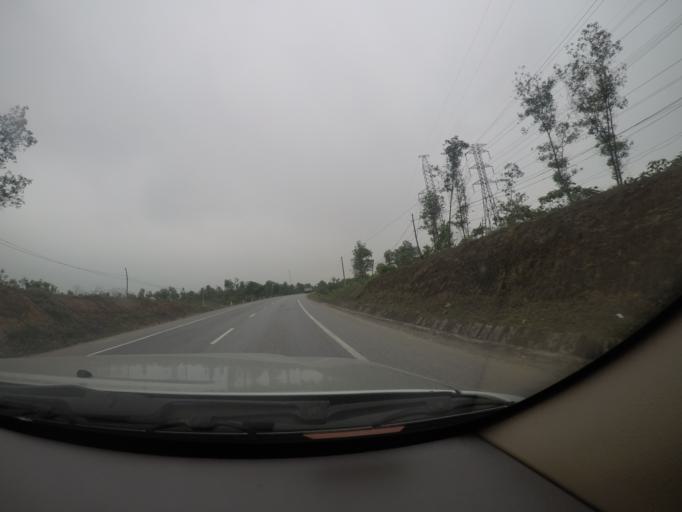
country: VN
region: Ha Tinh
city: Ky Anh
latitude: 18.0282
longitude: 106.3439
